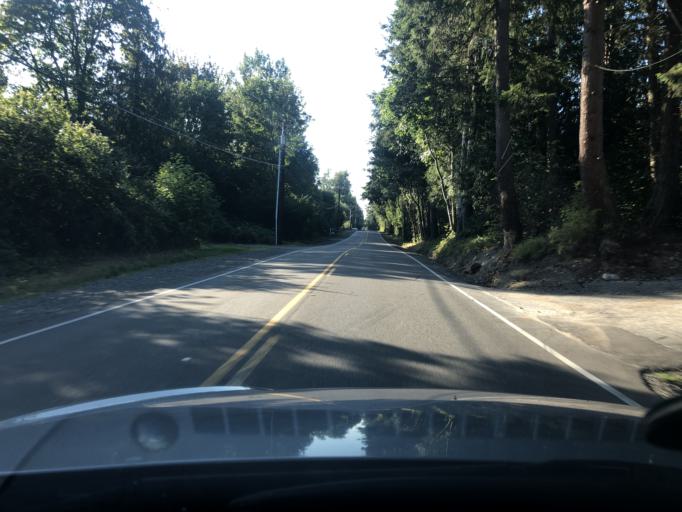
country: US
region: Washington
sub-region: Pierce County
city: Bonney Lake
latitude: 47.2395
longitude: -122.1448
